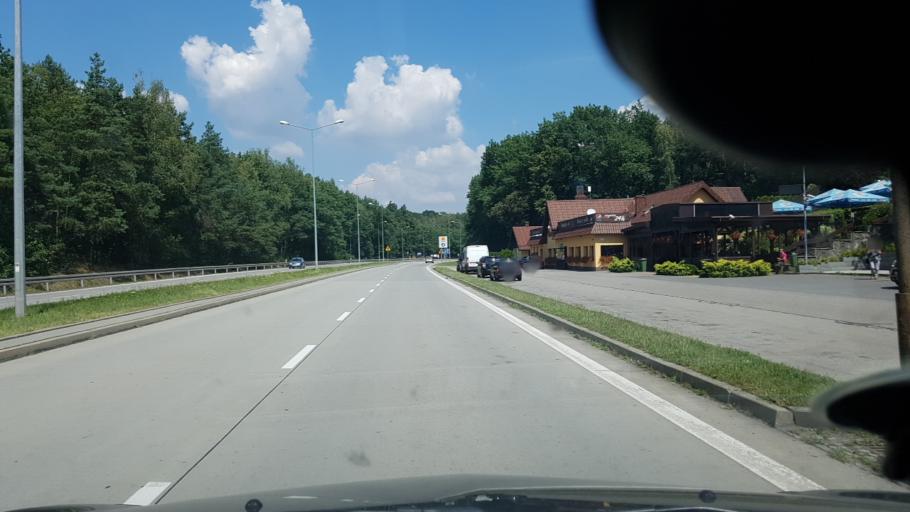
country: PL
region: Silesian Voivodeship
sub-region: Zory
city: Zory
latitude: 50.0594
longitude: 18.7226
